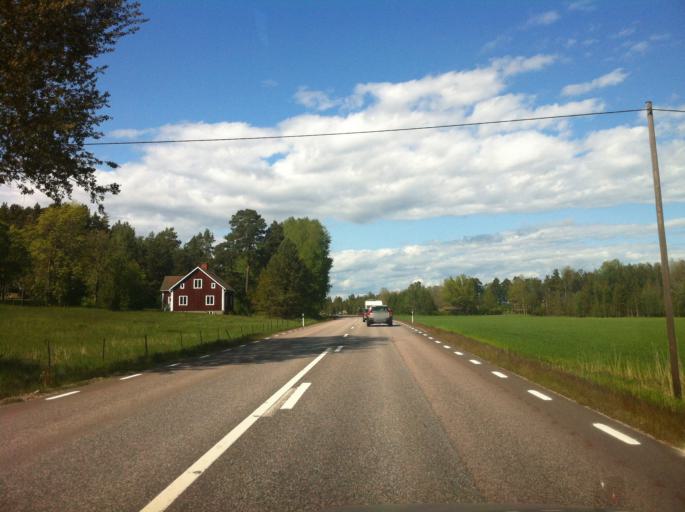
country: SE
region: Vaermland
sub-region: Kristinehamns Kommun
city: Bjorneborg
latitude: 59.1285
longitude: 14.1765
